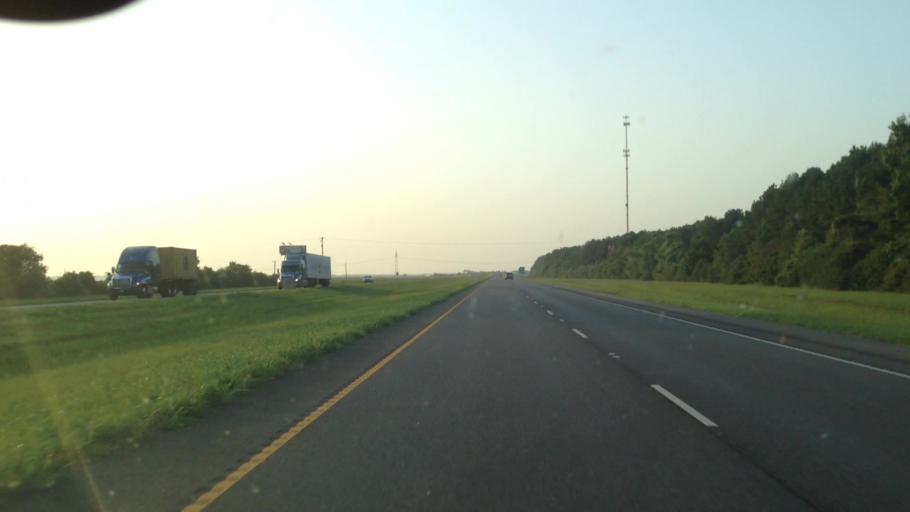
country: US
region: Louisiana
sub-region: Red River Parish
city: Coushatta
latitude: 31.8446
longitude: -93.2907
